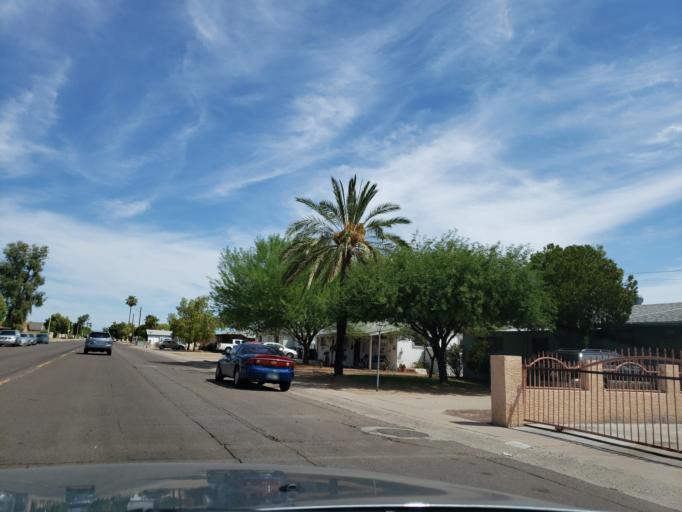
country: US
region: Arizona
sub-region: Maricopa County
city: Glendale
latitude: 33.5555
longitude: -112.1256
